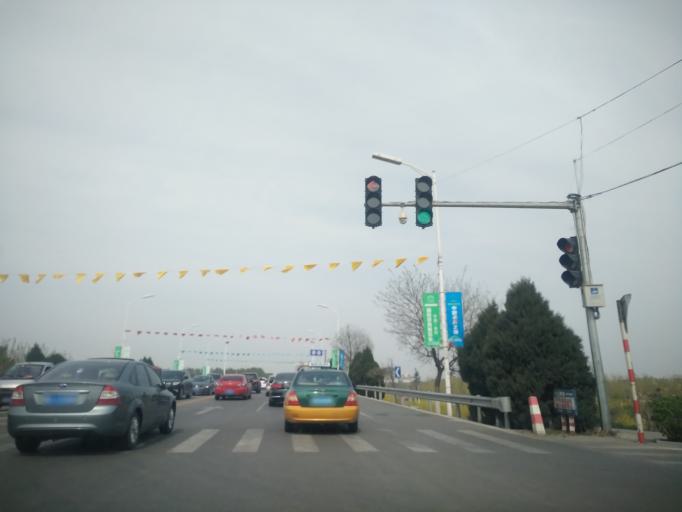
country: CN
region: Beijing
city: Xiji
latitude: 39.7774
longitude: 116.9807
